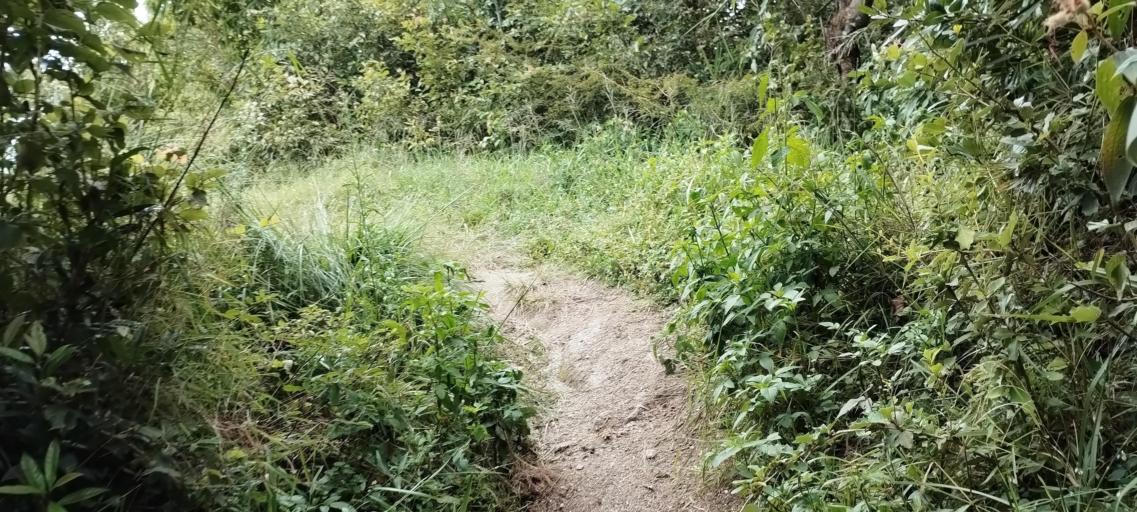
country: NP
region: Central Region
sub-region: Bagmati Zone
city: Kathmandu
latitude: 27.7875
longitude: 85.3755
